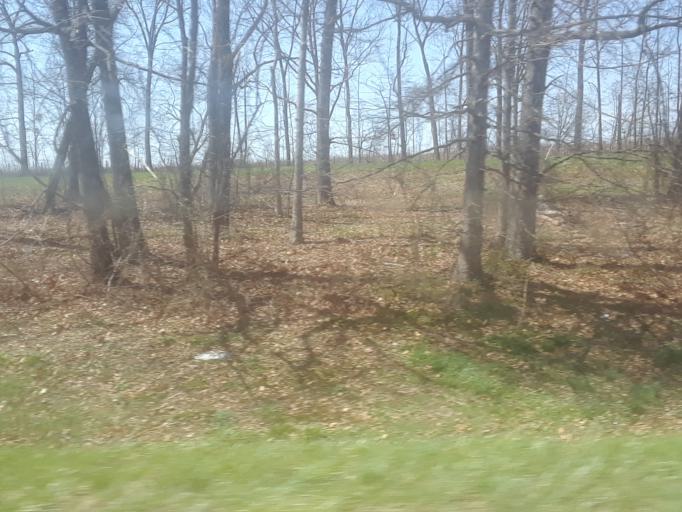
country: US
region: Virginia
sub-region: Shenandoah County
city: Mount Jackson
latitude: 38.7883
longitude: -78.6101
